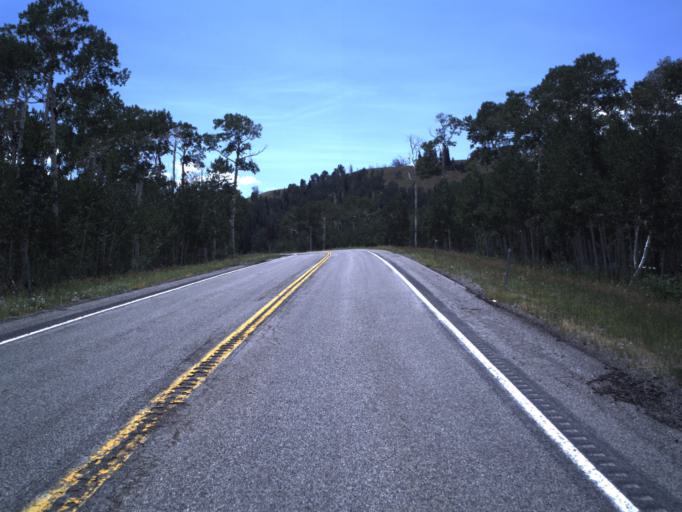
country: US
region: Utah
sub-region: Sanpete County
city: Fairview
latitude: 39.6574
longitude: -111.3290
